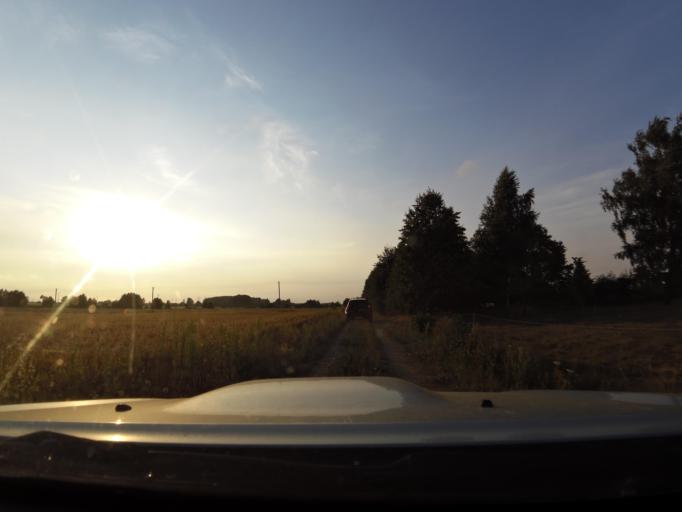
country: LT
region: Klaipedos apskritis
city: Silute
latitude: 55.4734
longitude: 21.4693
